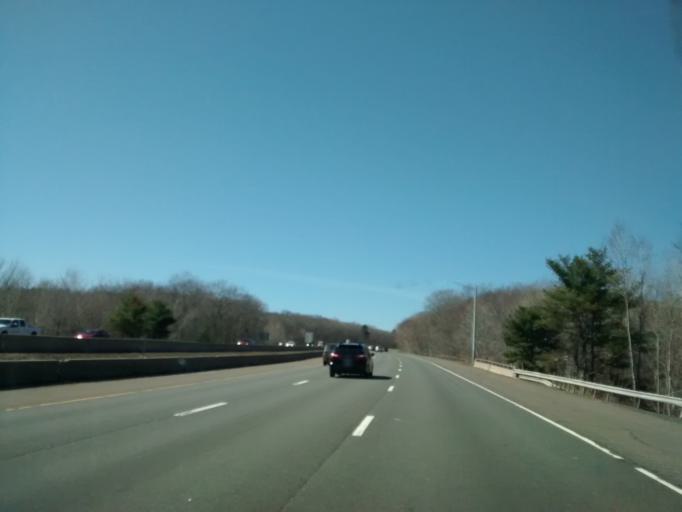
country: US
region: Connecticut
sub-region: Tolland County
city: Tolland
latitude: 41.8607
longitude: -72.3683
